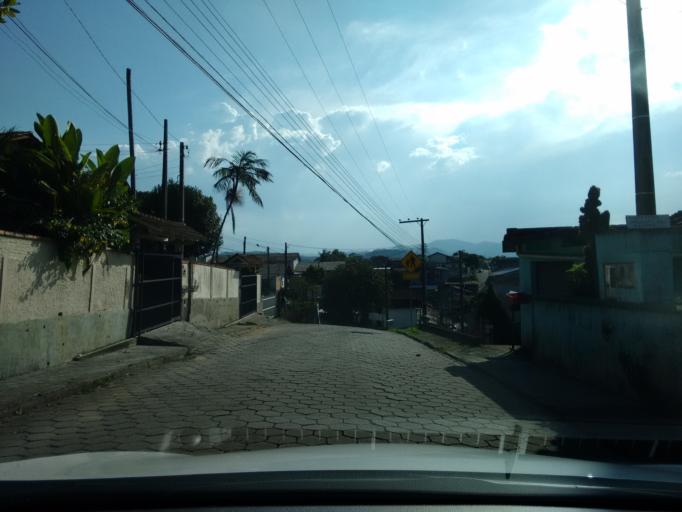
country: BR
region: Santa Catarina
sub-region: Blumenau
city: Blumenau
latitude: -26.8710
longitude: -49.0806
